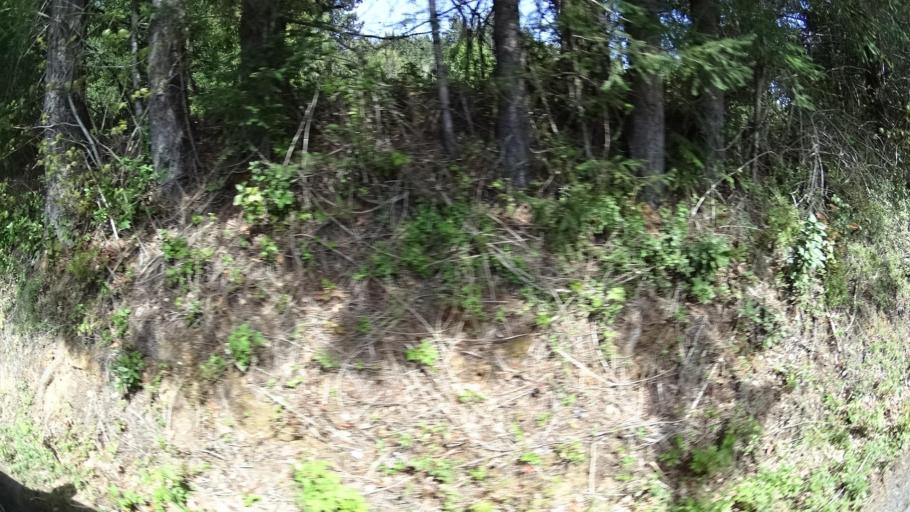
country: US
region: California
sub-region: Humboldt County
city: Redway
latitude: 40.3778
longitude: -123.7426
